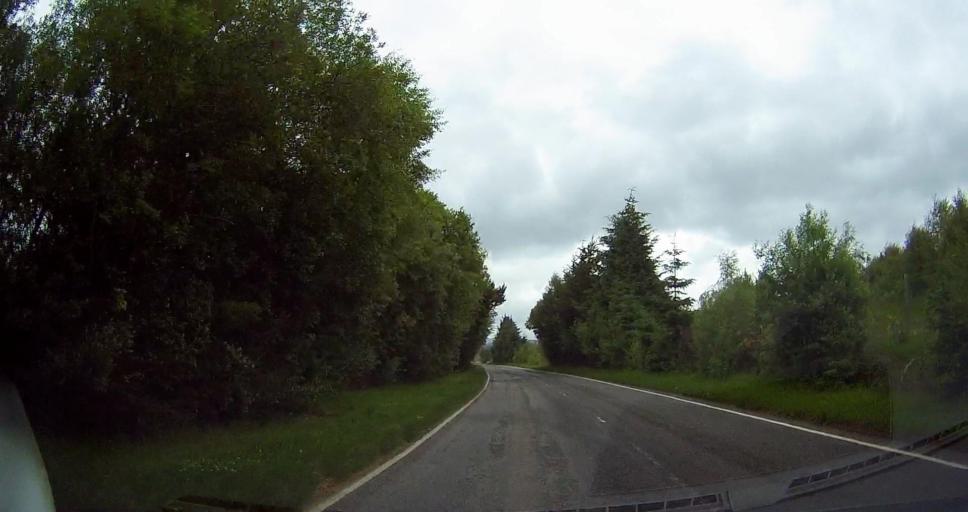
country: GB
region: Scotland
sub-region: Highland
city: Alness
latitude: 58.0446
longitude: -4.4231
